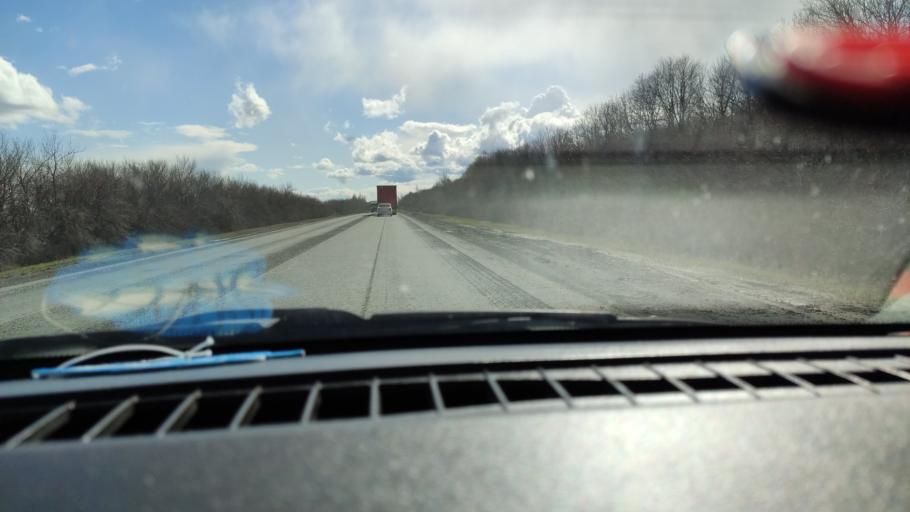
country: RU
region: Saratov
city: Dukhovnitskoye
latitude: 52.6426
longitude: 48.1932
